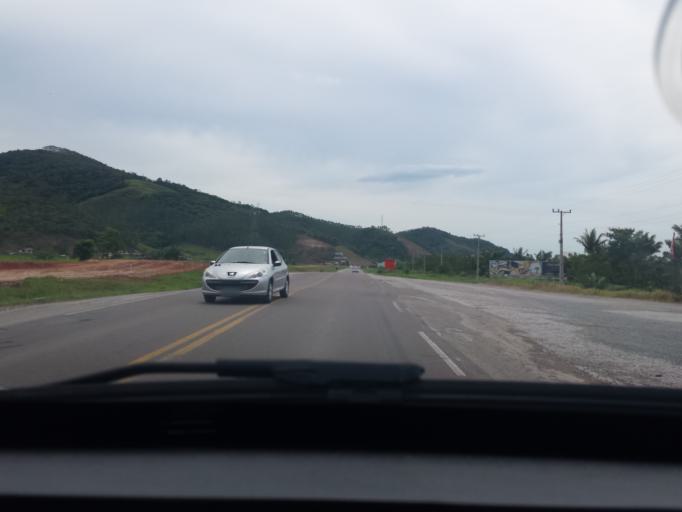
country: BR
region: Santa Catarina
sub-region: Gaspar
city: Gaspar
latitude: -26.8985
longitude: -48.9255
